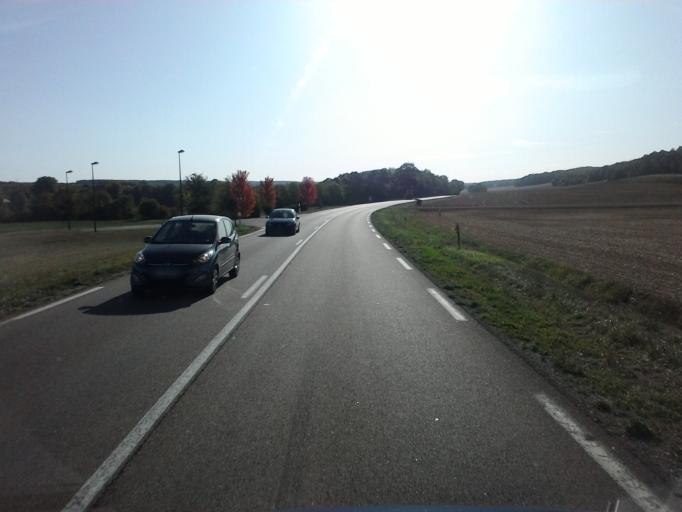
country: FR
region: Champagne-Ardenne
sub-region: Departement de l'Aube
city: Bar-sur-Seine
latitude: 48.1334
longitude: 4.3326
